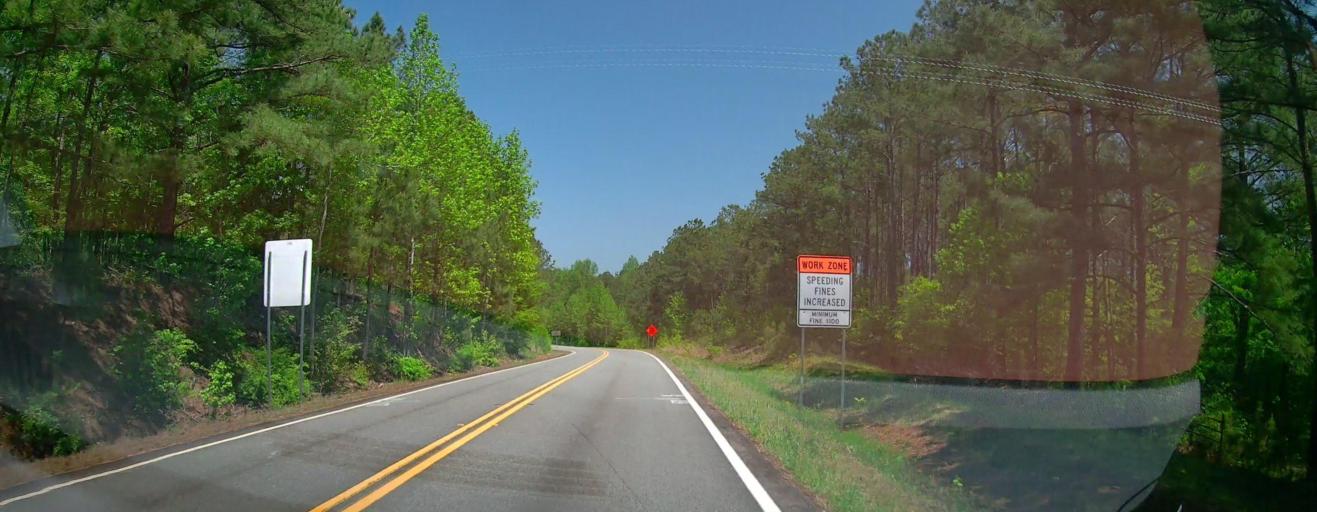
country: US
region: Georgia
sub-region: Jasper County
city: Monticello
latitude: 33.2976
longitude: -83.6375
